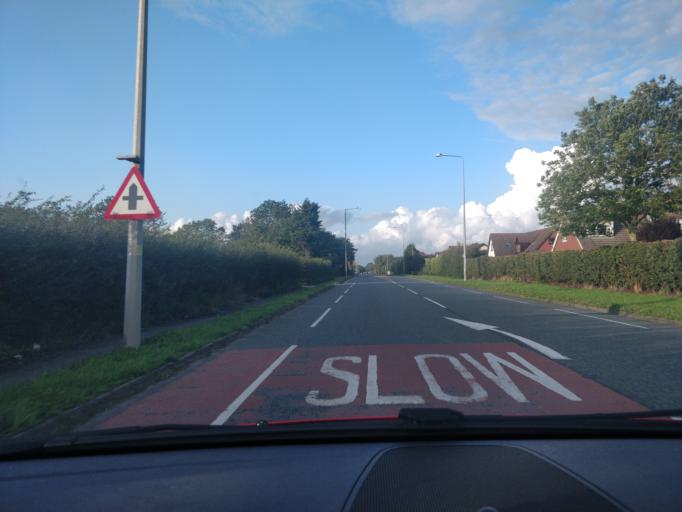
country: GB
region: England
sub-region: Lancashire
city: Tarleton
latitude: 53.7020
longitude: -2.8037
